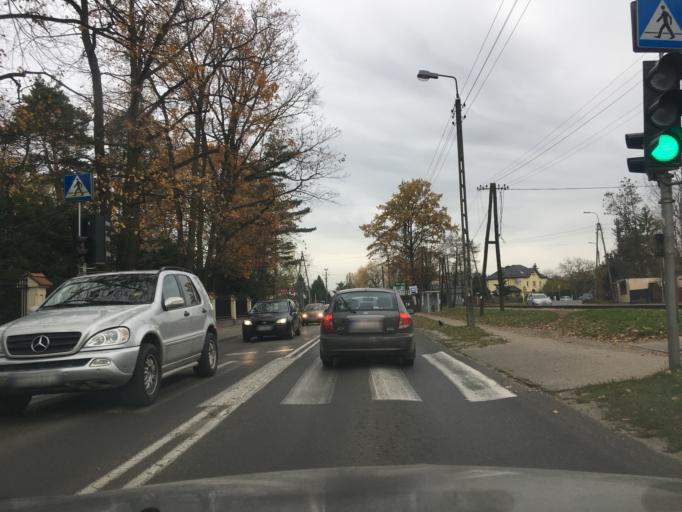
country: PL
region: Masovian Voivodeship
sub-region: Powiat piaseczynski
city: Piaseczno
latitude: 52.0574
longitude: 21.0084
